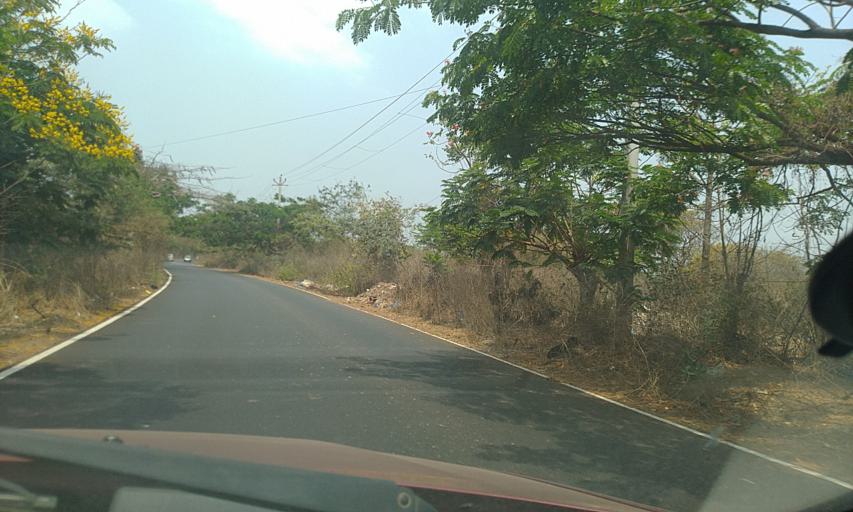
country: IN
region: Goa
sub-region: North Goa
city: Mapuca
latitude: 15.6085
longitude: 73.7994
